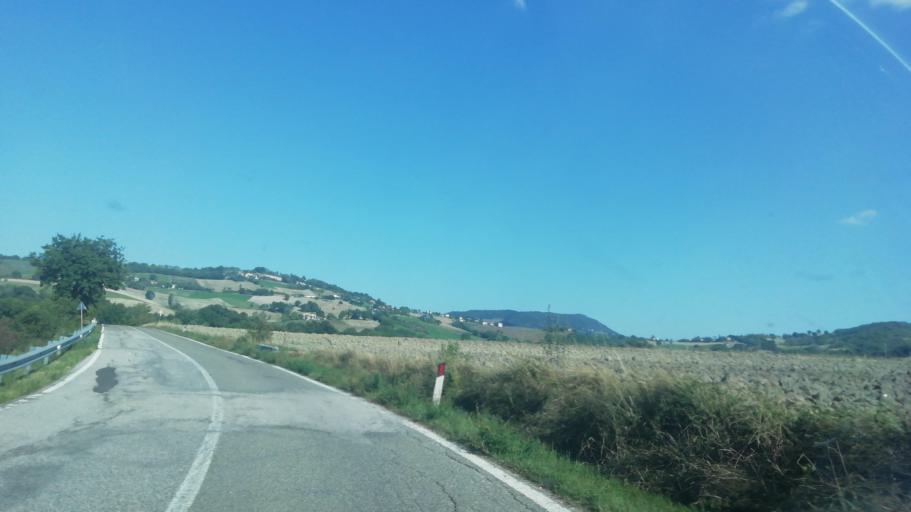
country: IT
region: The Marches
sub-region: Provincia di Pesaro e Urbino
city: Frontone
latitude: 43.5394
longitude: 12.7100
